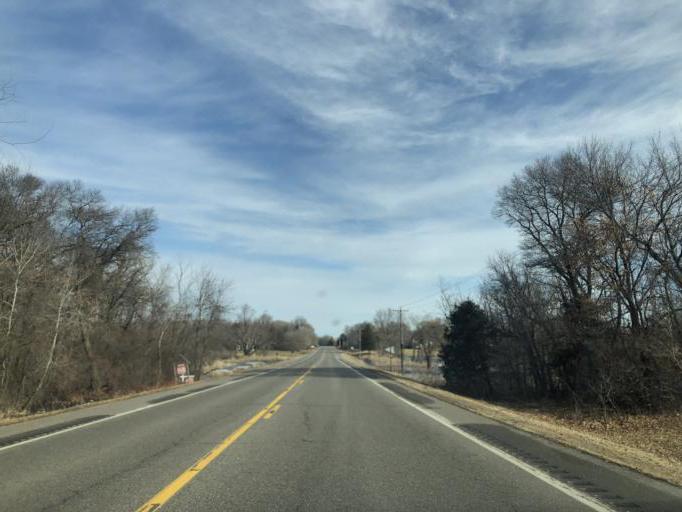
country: US
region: Minnesota
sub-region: Sherburne County
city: Becker
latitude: 45.4125
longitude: -93.8708
